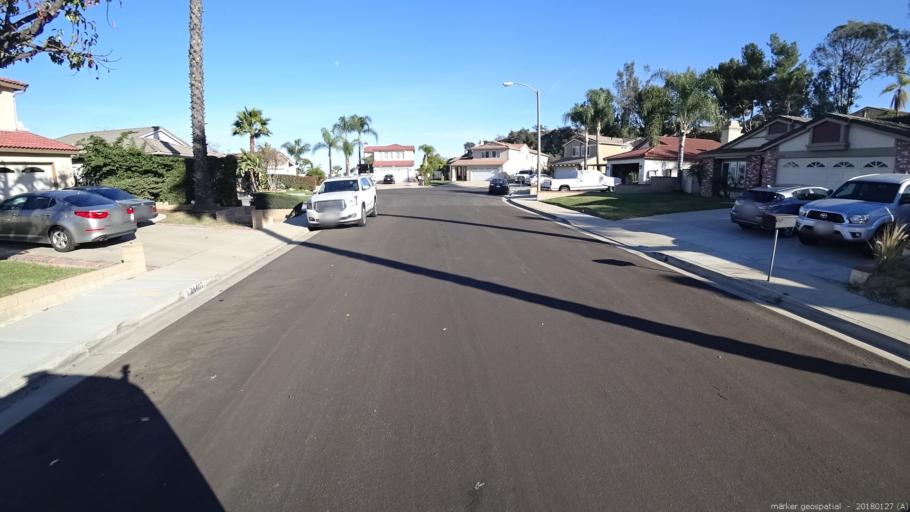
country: US
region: California
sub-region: Los Angeles County
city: Diamond Bar
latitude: 34.0209
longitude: -117.7874
